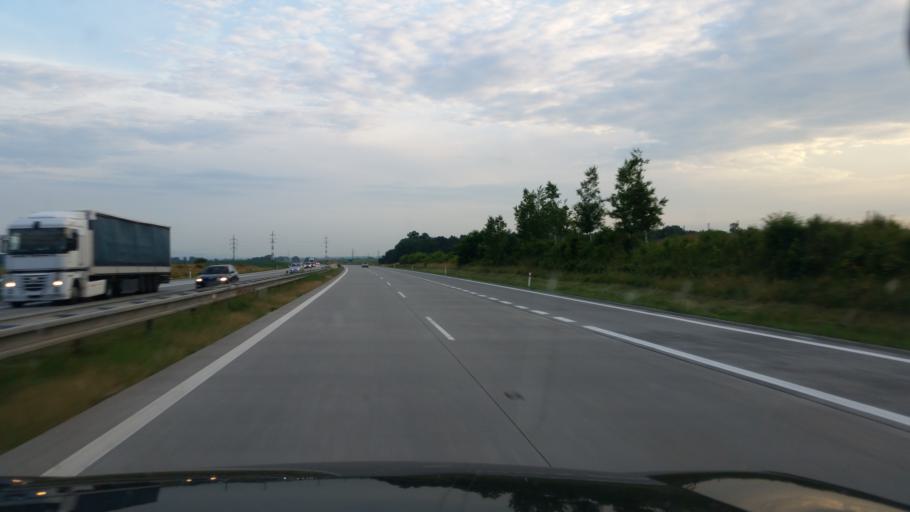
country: CZ
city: Bilovec
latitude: 49.7261
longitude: 18.0150
